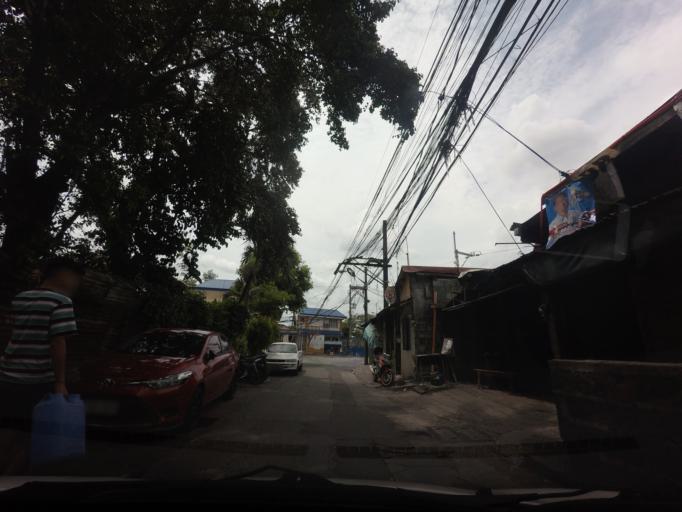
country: PH
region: Metro Manila
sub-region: Marikina
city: Calumpang
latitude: 14.5944
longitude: 121.0907
